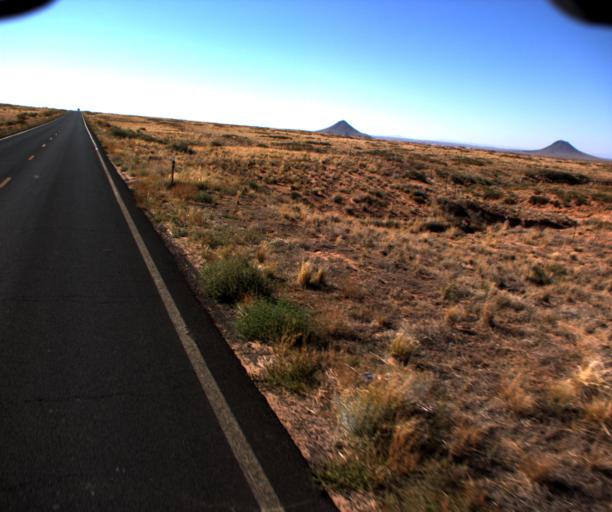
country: US
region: Arizona
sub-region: Navajo County
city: Dilkon
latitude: 35.4288
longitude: -110.4257
